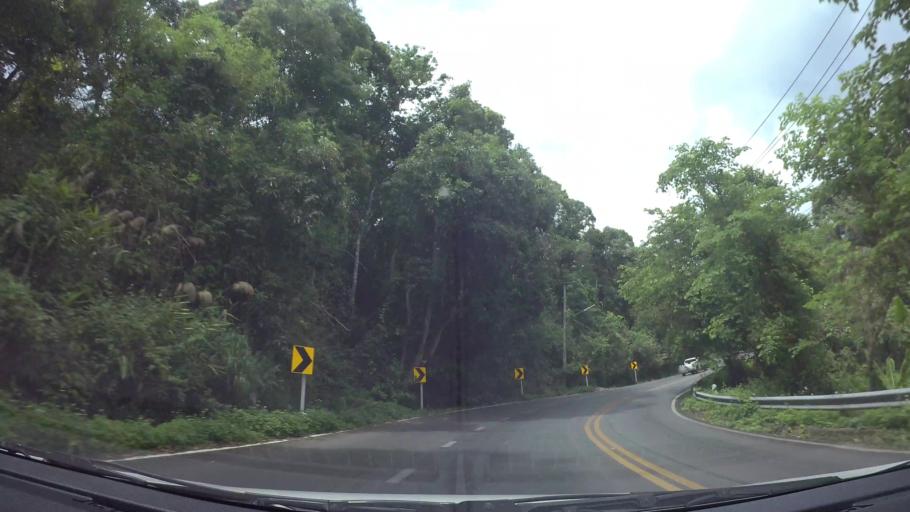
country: TH
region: Chiang Mai
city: Chiang Mai
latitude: 18.7935
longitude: 98.9214
